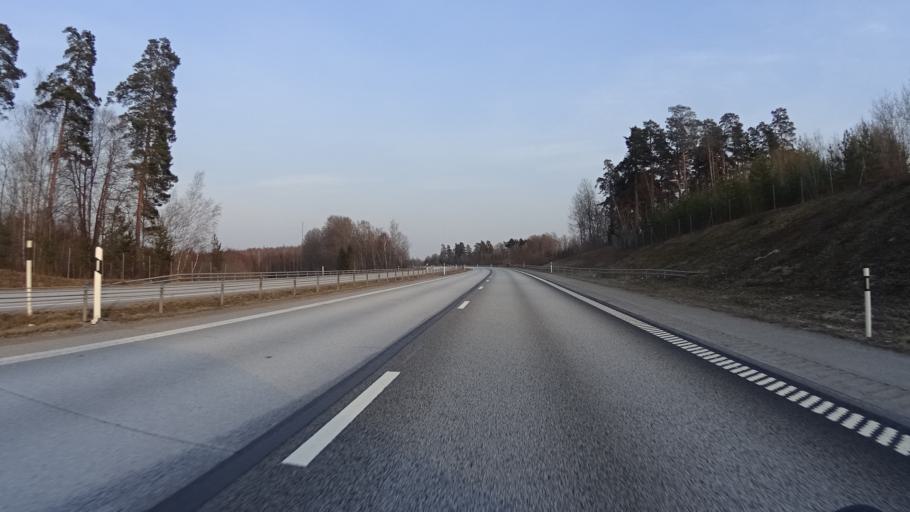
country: SE
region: Soedermanland
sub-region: Eskilstuna Kommun
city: Arla
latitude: 59.3766
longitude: 16.7964
